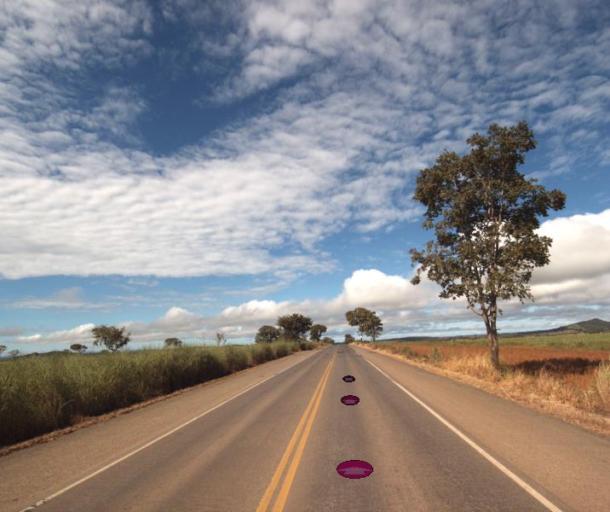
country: BR
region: Goias
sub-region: Uruacu
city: Uruacu
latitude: -14.7061
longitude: -49.2224
